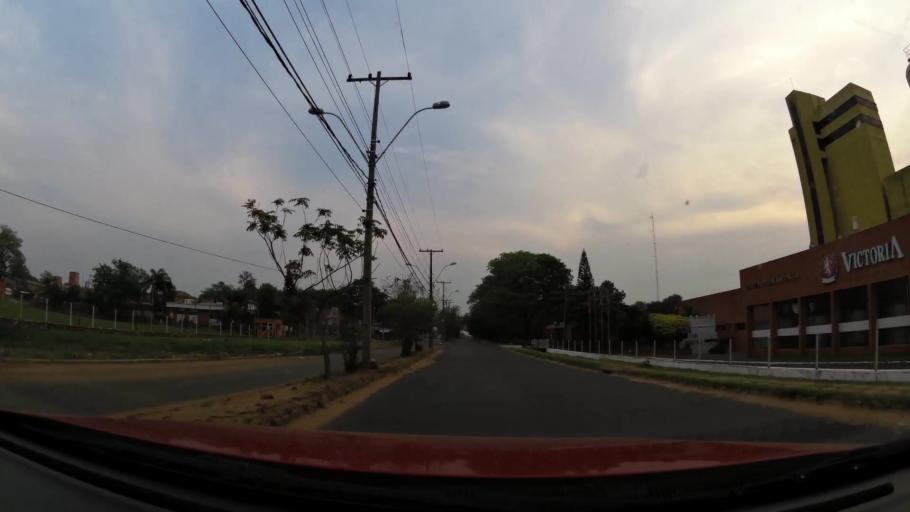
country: PY
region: Central
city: Lambare
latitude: -25.3517
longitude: -57.6416
